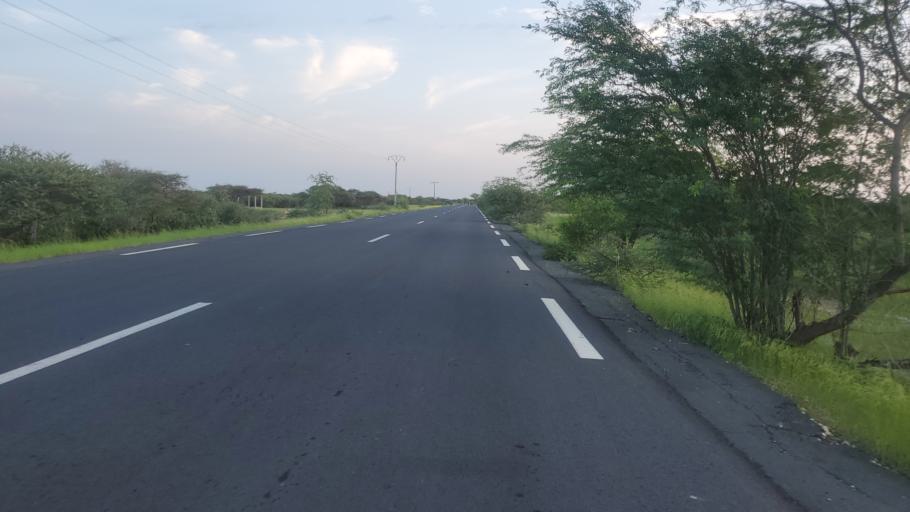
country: SN
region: Saint-Louis
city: Saint-Louis
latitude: 16.1246
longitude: -16.4137
